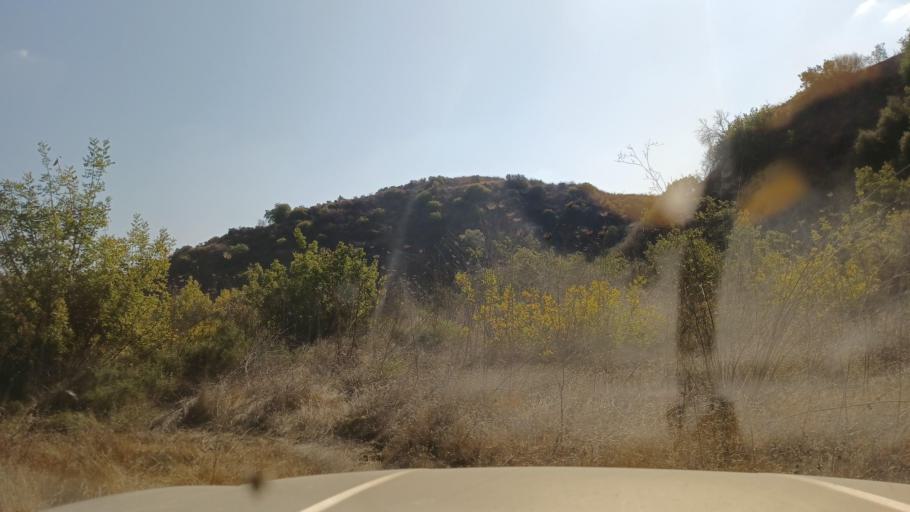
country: CY
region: Pafos
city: Pegeia
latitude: 34.9194
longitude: 32.4580
